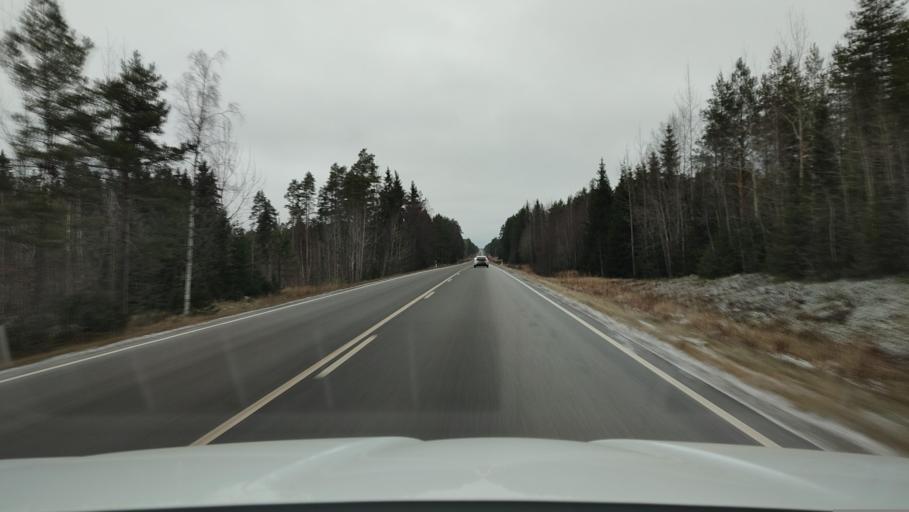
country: FI
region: Ostrobothnia
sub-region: Sydosterbotten
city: Naerpes
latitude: 62.5790
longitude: 21.4926
